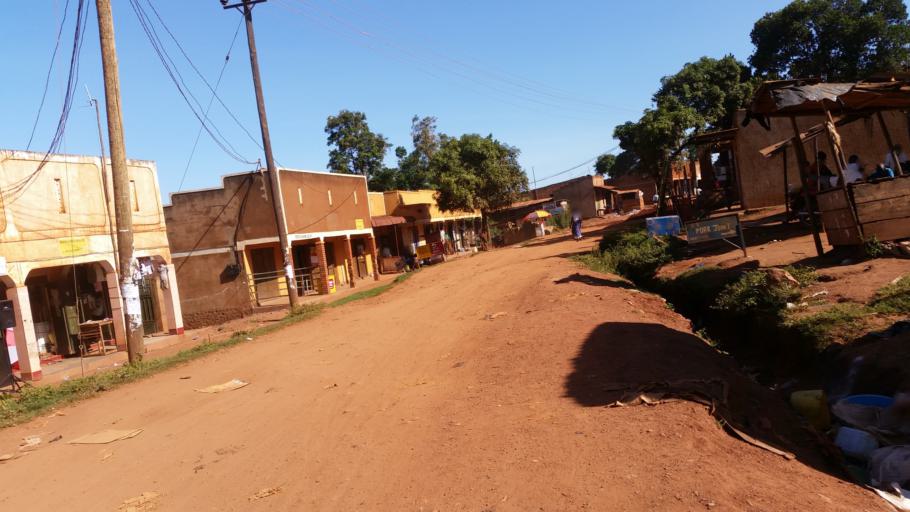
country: UG
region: Central Region
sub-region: Wakiso District
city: Kireka
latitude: 0.3362
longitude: 32.6538
